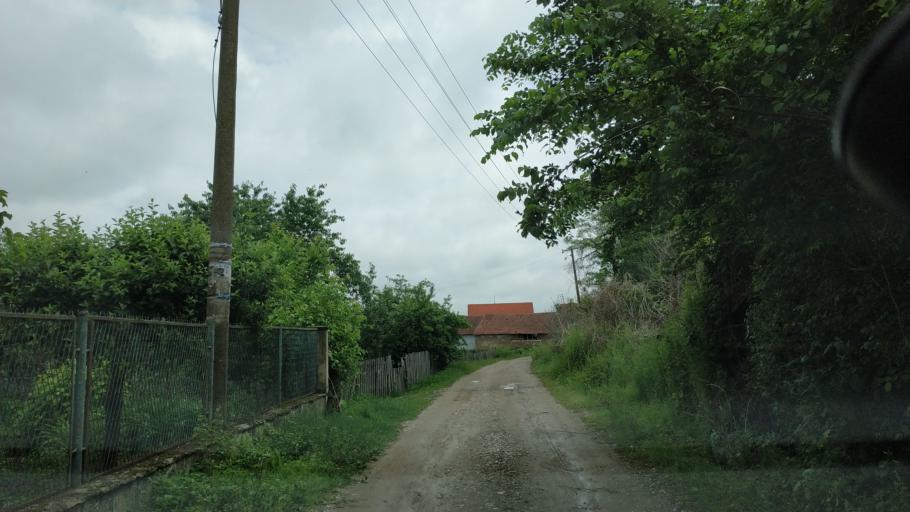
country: RS
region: Central Serbia
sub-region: Nisavski Okrug
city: Aleksinac
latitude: 43.4302
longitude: 21.6530
